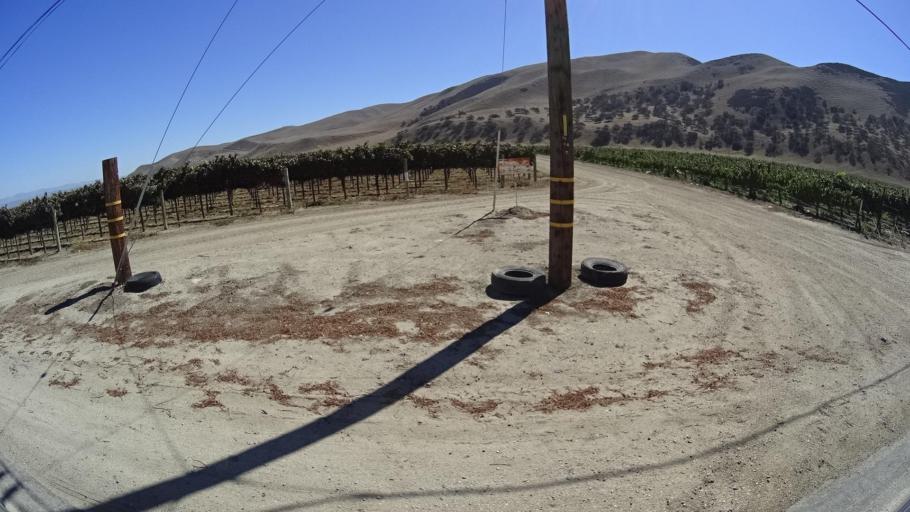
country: US
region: California
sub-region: Monterey County
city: Greenfield
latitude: 36.2901
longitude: -121.2916
